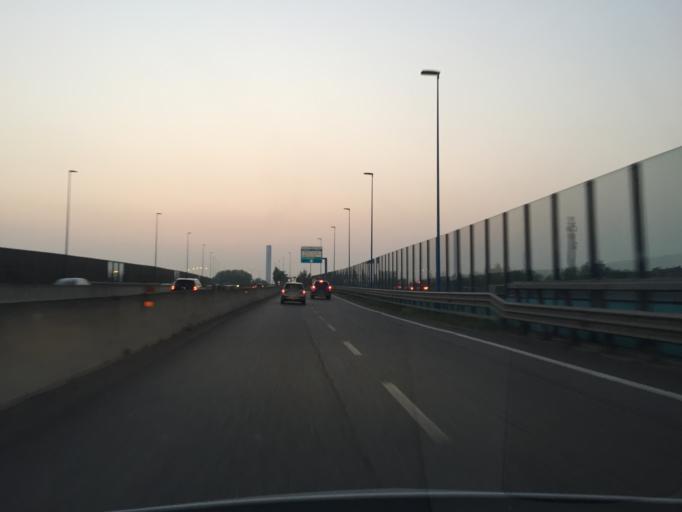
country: IT
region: Lombardy
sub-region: Provincia di Brescia
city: San Zeno Naviglio
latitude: 45.5102
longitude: 10.2298
